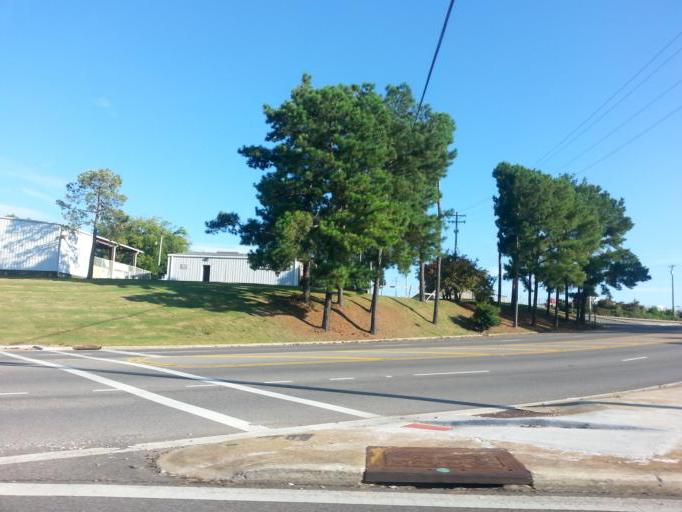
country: US
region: Alabama
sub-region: Lauderdale County
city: Florence
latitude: 34.8034
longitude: -87.6681
